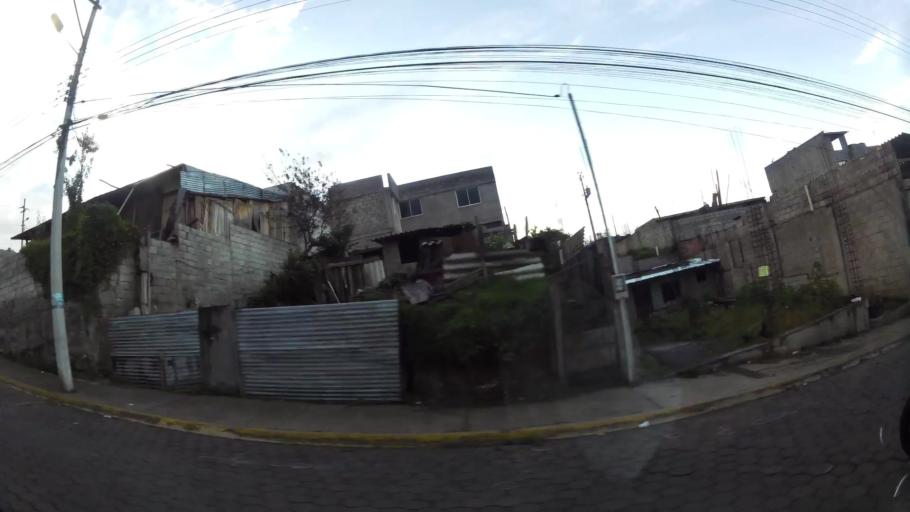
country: EC
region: Pichincha
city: Quito
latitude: -0.1024
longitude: -78.5240
